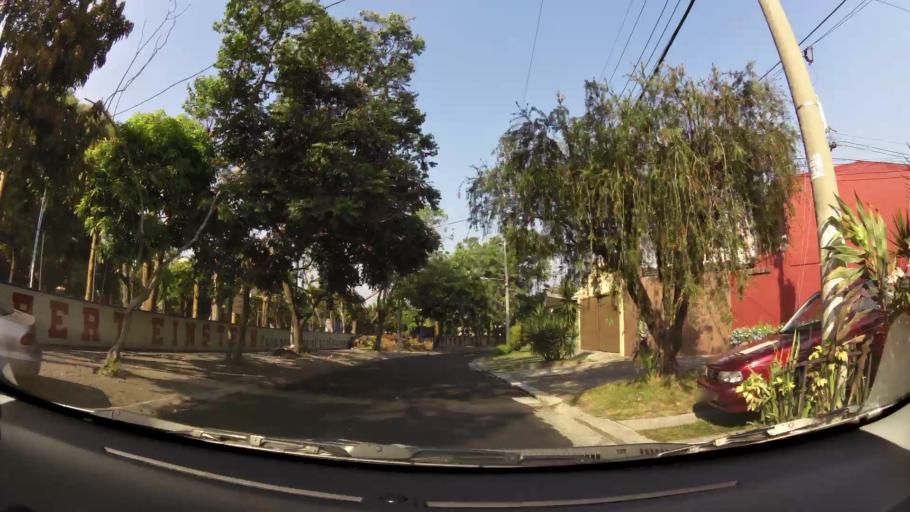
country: SV
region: La Libertad
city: Antiguo Cuscatlan
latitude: 13.6743
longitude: -89.2346
